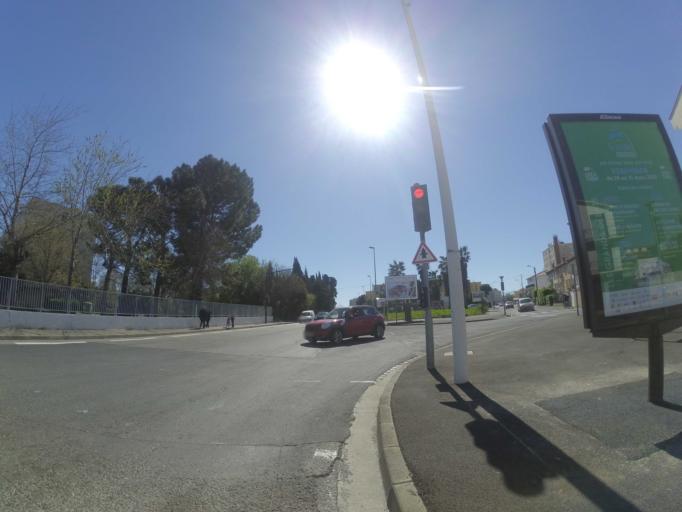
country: FR
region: Languedoc-Roussillon
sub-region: Departement des Pyrenees-Orientales
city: Perpignan
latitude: 42.7128
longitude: 2.8955
